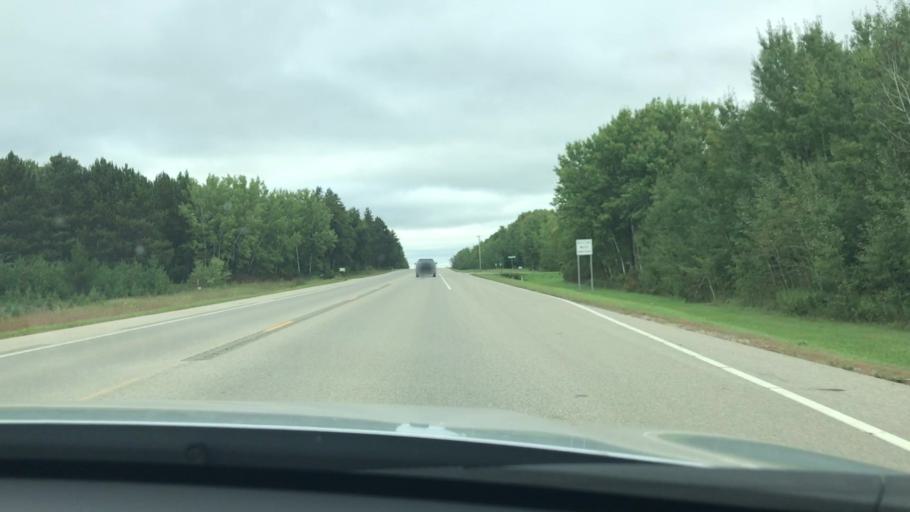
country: US
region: Minnesota
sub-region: Hubbard County
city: Park Rapids
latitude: 46.8458
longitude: -95.0820
